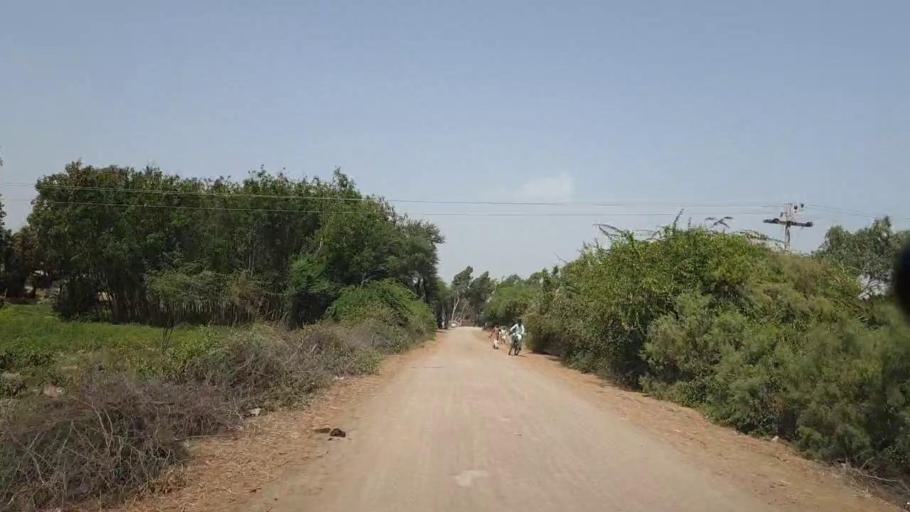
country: PK
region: Sindh
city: Matli
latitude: 25.0752
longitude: 68.7065
